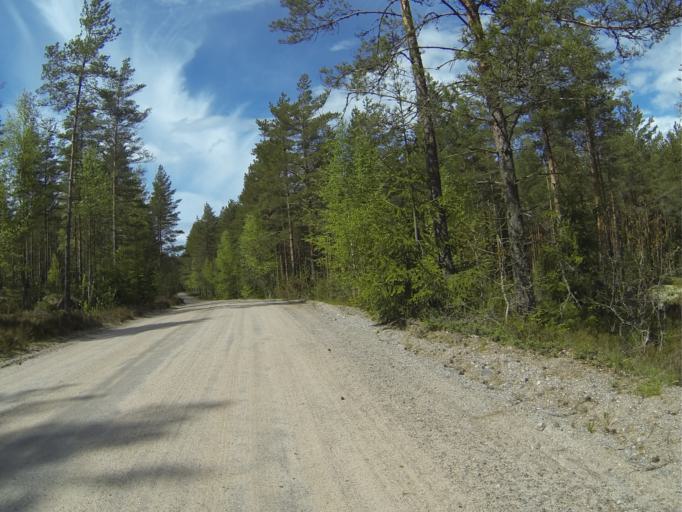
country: FI
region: Varsinais-Suomi
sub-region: Salo
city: Halikko
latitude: 60.3230
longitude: 23.0719
